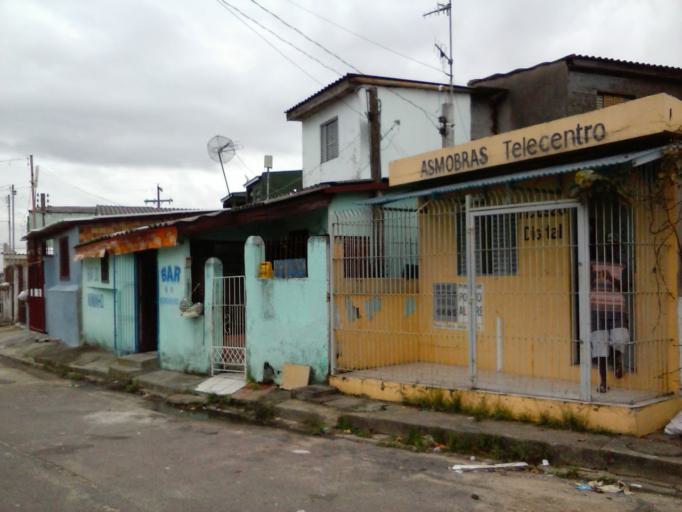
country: BR
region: Rio Grande do Sul
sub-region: Porto Alegre
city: Porto Alegre
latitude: -30.0450
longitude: -51.1498
